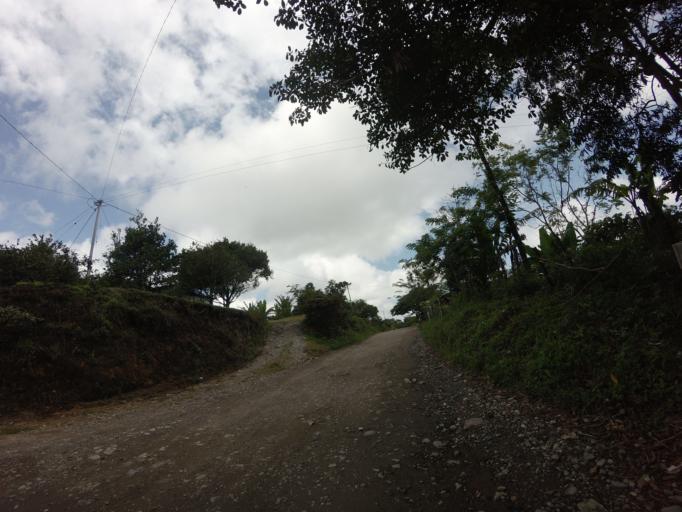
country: CO
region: Caldas
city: Victoria
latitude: 5.3245
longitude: -74.9324
